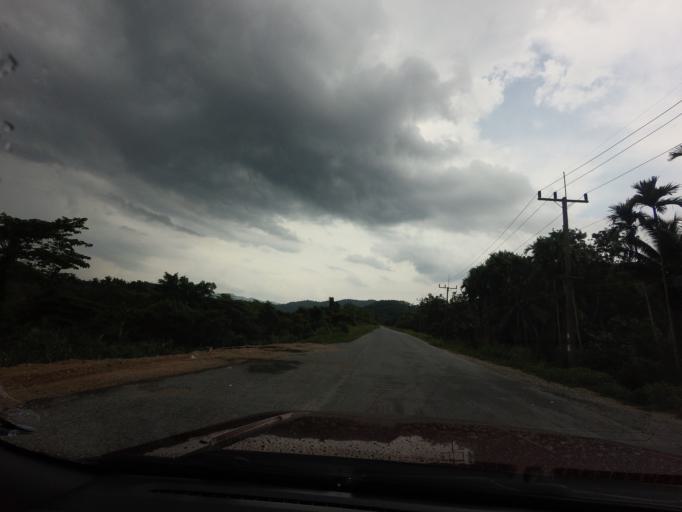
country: TH
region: Yala
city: Ban Nang Sata
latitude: 6.2236
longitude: 101.2253
